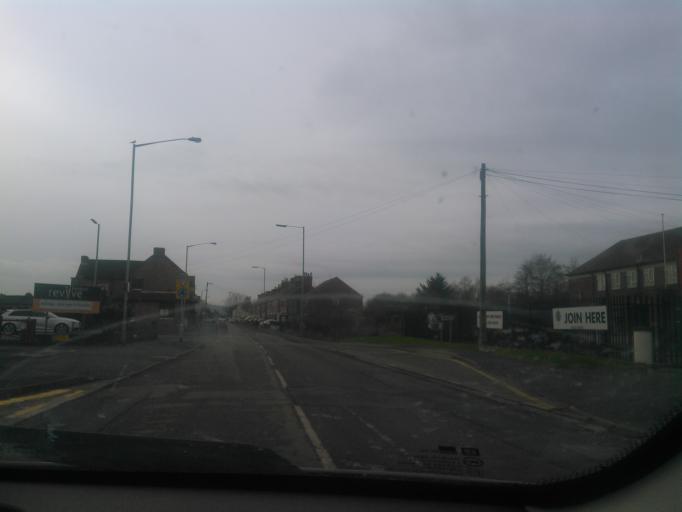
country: GB
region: England
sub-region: Telford and Wrekin
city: Oakengates
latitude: 52.7170
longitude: -2.4466
